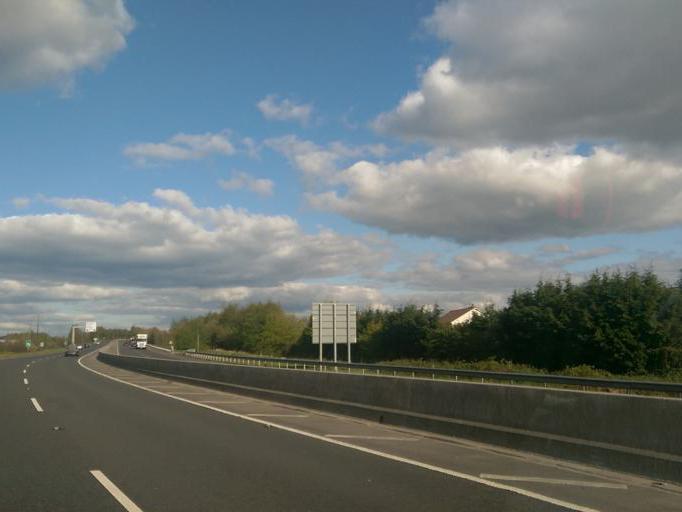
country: IE
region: Leinster
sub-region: An Iarmhi
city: Athlone
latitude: 53.4344
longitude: -7.9506
